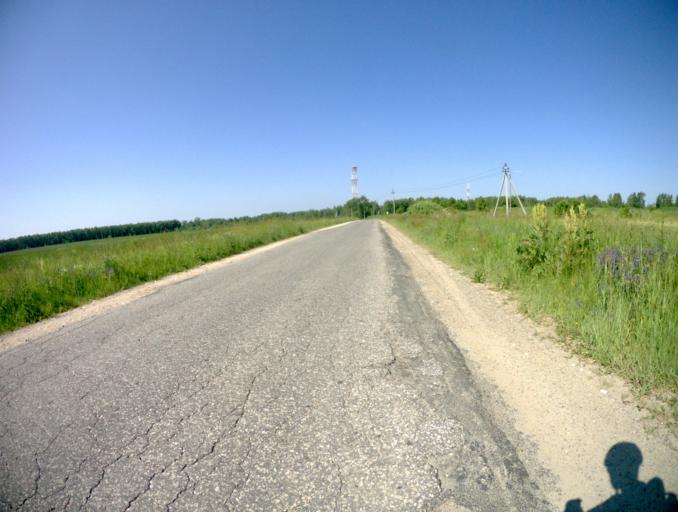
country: RU
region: Vladimir
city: Novovyazniki
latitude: 56.2322
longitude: 42.2198
